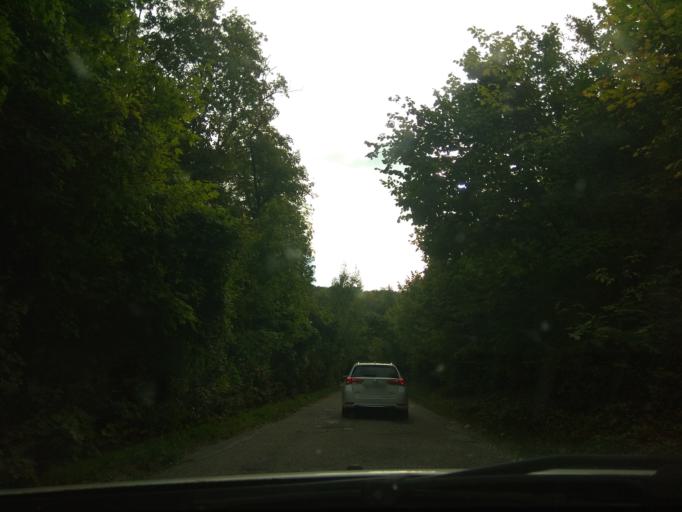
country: HU
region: Borsod-Abauj-Zemplen
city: Miskolc
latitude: 48.0672
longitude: 20.6803
